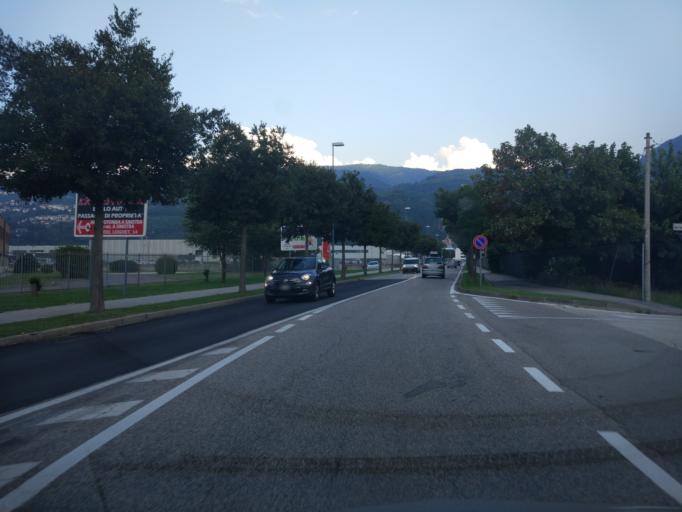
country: IT
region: Trentino-Alto Adige
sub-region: Provincia di Trento
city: Meano
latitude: 46.1187
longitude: 11.0977
